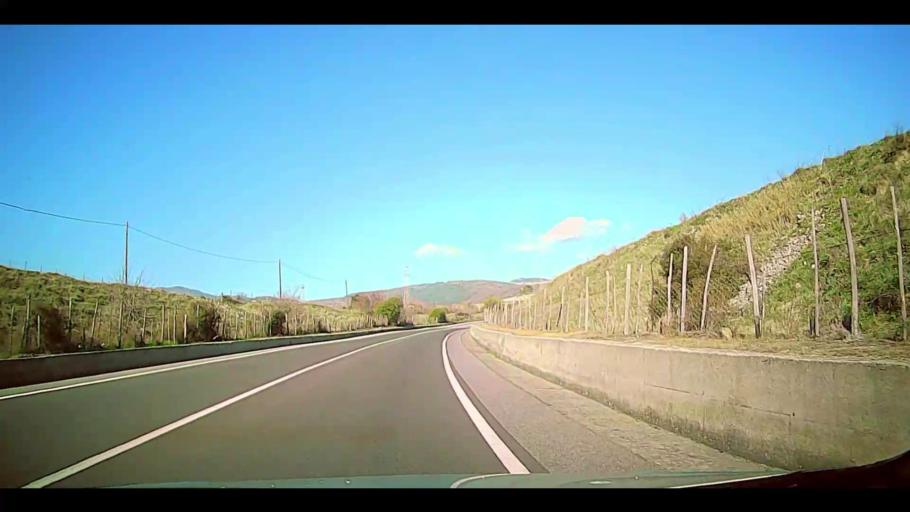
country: IT
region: Calabria
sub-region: Provincia di Crotone
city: Cotronei
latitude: 39.1868
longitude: 16.8184
